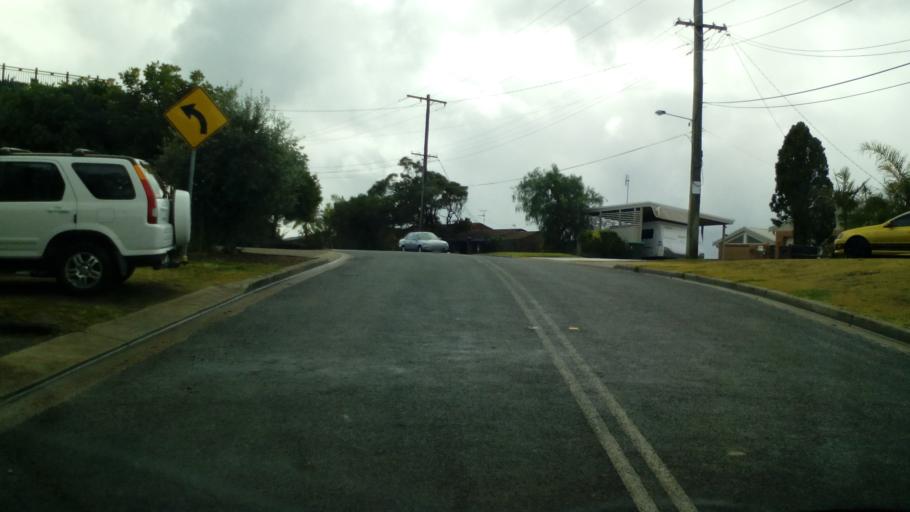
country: AU
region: New South Wales
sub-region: Lake Macquarie Shire
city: Belmont South
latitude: -33.1123
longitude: 151.6409
